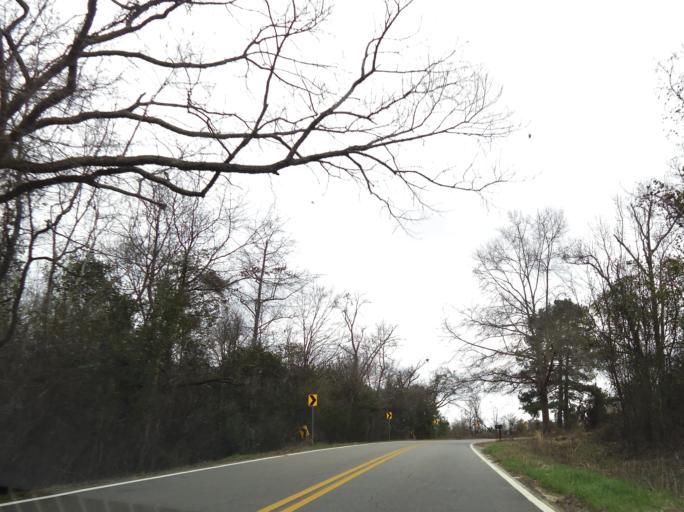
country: US
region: Georgia
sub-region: Twiggs County
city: Jeffersonville
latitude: 32.5598
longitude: -83.3717
